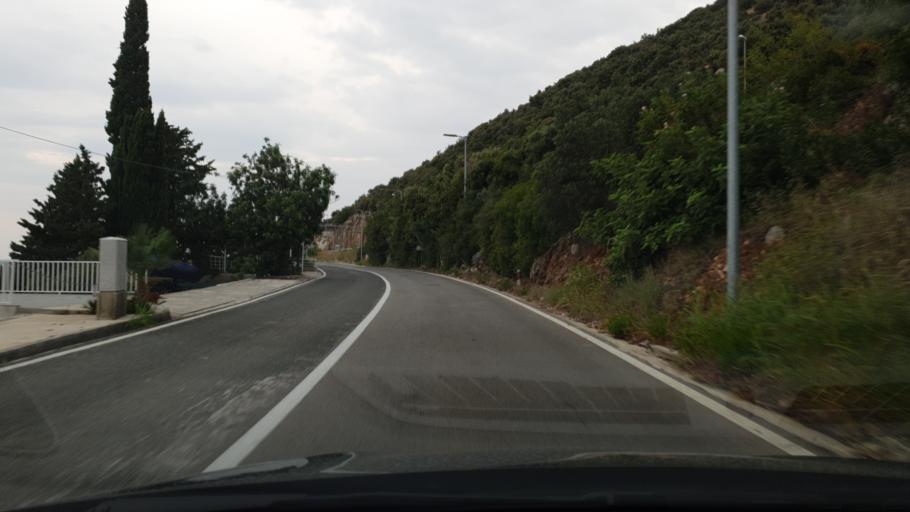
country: HR
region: Dubrovacko-Neretvanska
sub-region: Grad Dubrovnik
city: Mokosica
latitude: 42.6749
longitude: 18.0641
